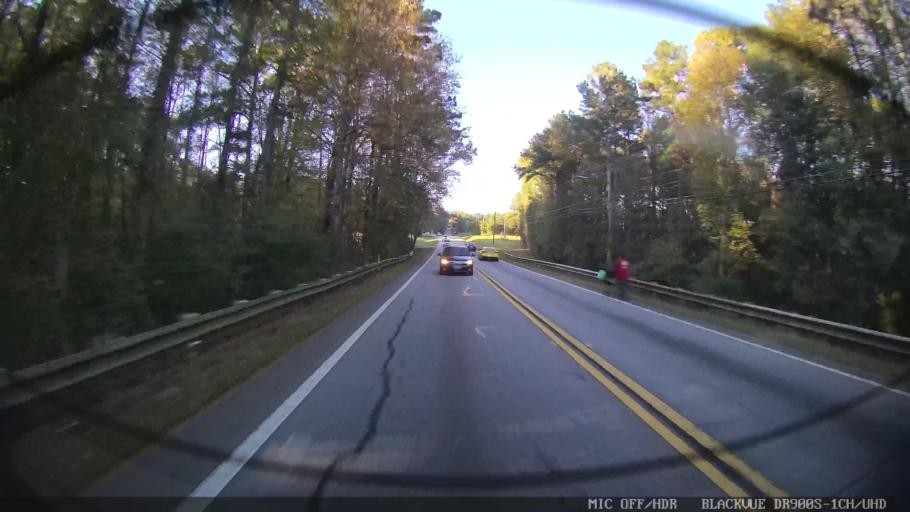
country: US
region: Georgia
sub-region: Henry County
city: Stockbridge
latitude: 33.5691
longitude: -84.2621
